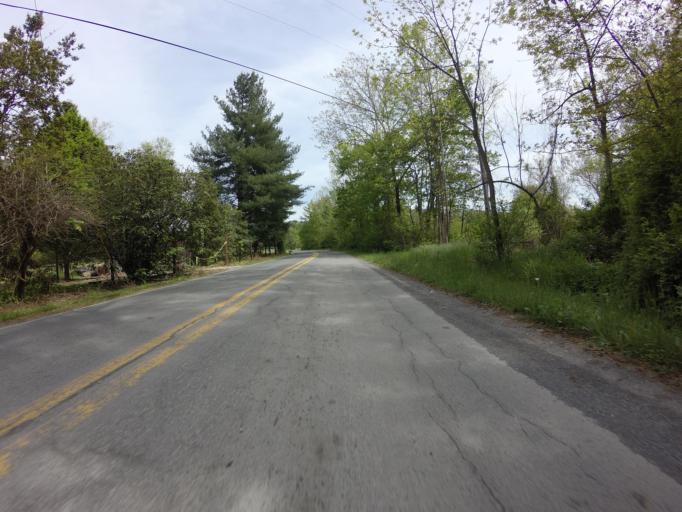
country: US
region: Maryland
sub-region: Carroll County
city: New Windsor
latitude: 39.4885
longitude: -77.0986
